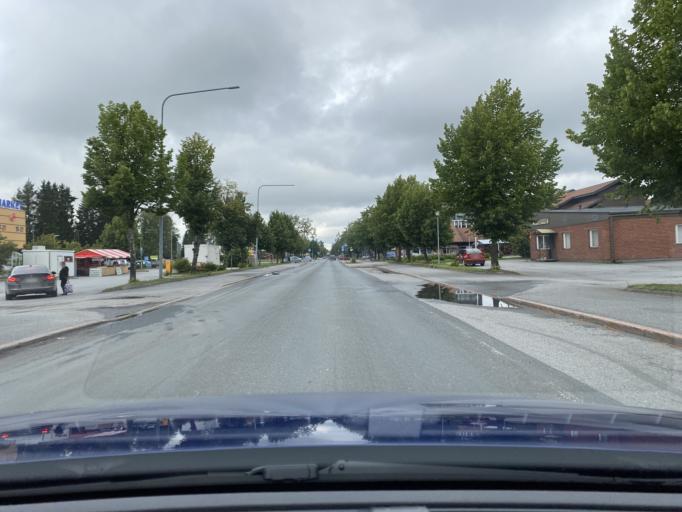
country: FI
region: Ostrobothnia
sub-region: Kyroenmaa
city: Laihia
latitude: 62.9791
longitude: 22.0093
